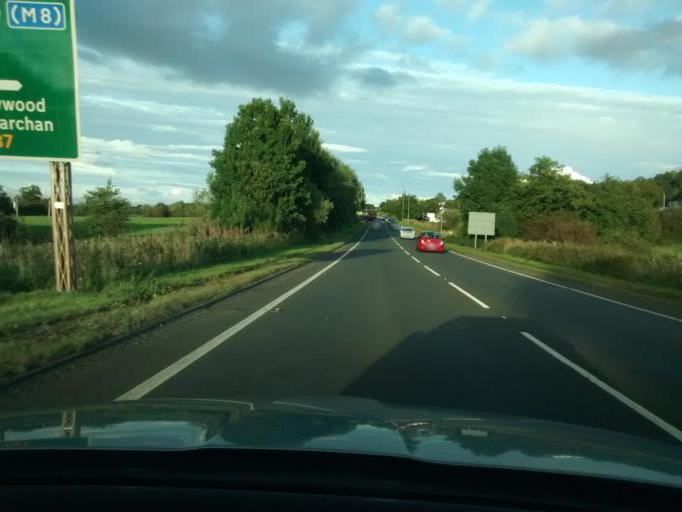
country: GB
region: Scotland
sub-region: Renfrewshire
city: Howwood
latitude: 55.8048
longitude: -4.5773
